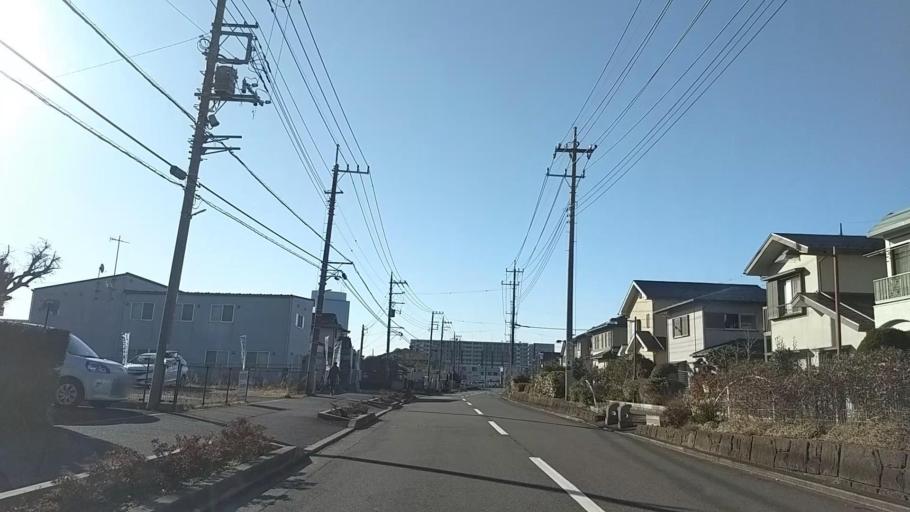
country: JP
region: Kanagawa
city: Atsugi
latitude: 35.4319
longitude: 139.3597
